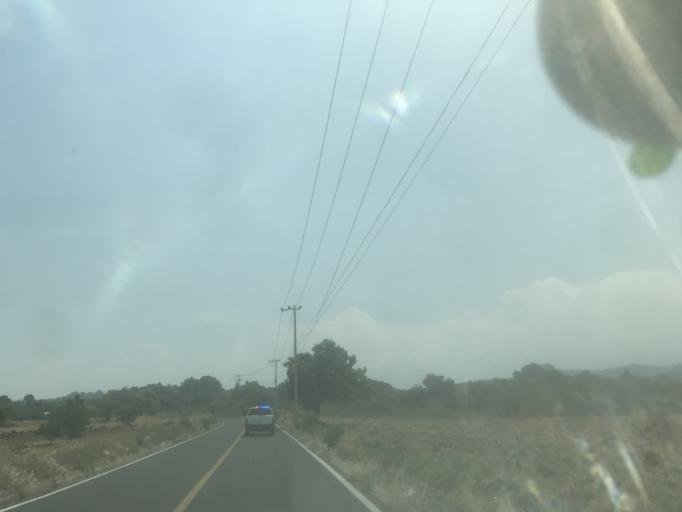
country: MX
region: Morelos
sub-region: Yecapixtla
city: Achichipico
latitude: 18.9587
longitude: -98.8286
